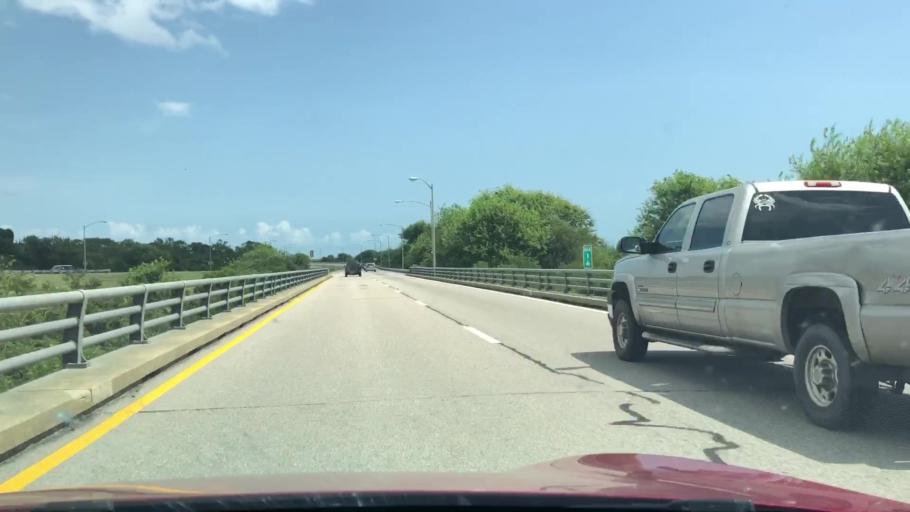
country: US
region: Virginia
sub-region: Northampton County
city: Cape Charles
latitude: 37.0917
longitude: -75.9778
